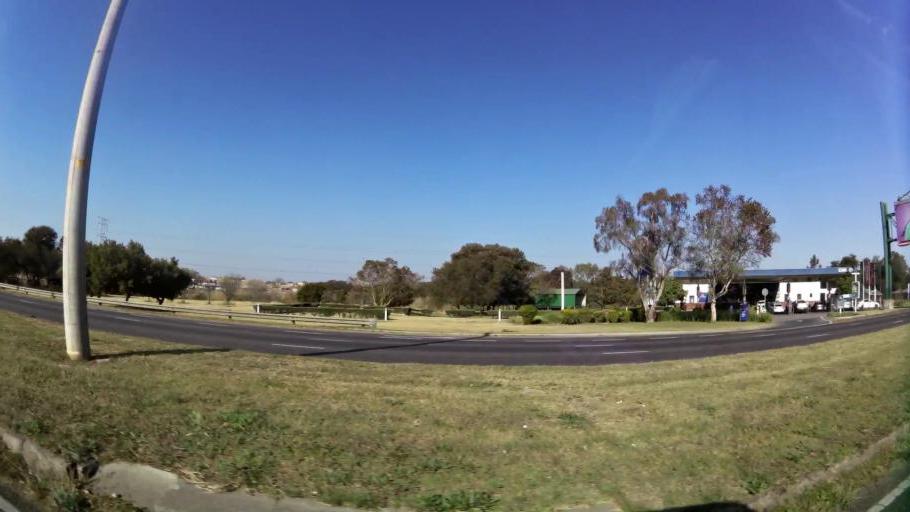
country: ZA
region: Gauteng
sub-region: City of Tshwane Metropolitan Municipality
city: Pretoria
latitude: -25.7150
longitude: 28.1700
